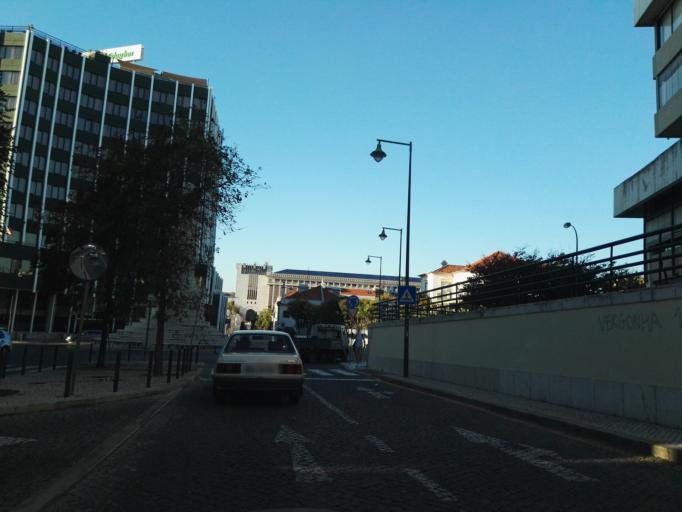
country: PT
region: Lisbon
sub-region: Lisbon
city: Lisbon
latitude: 38.7375
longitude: -9.1407
